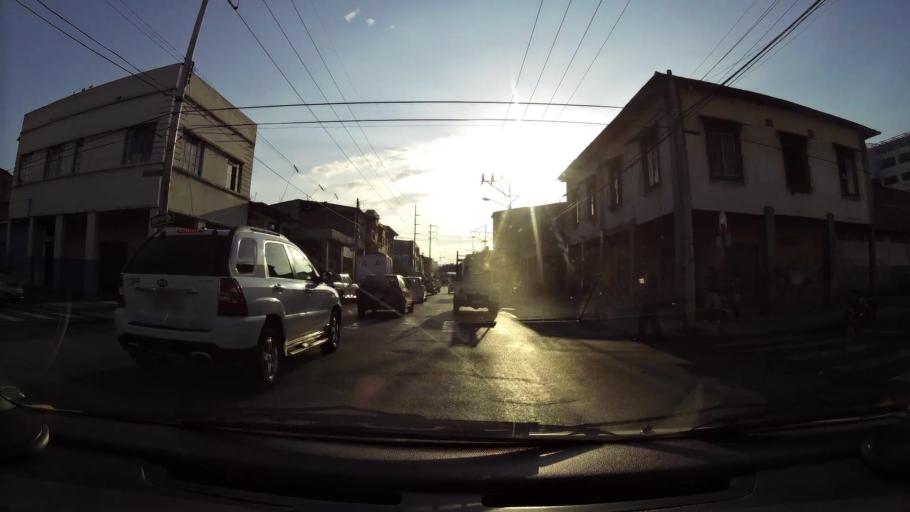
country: EC
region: Guayas
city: Guayaquil
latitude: -2.2080
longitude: -79.8935
